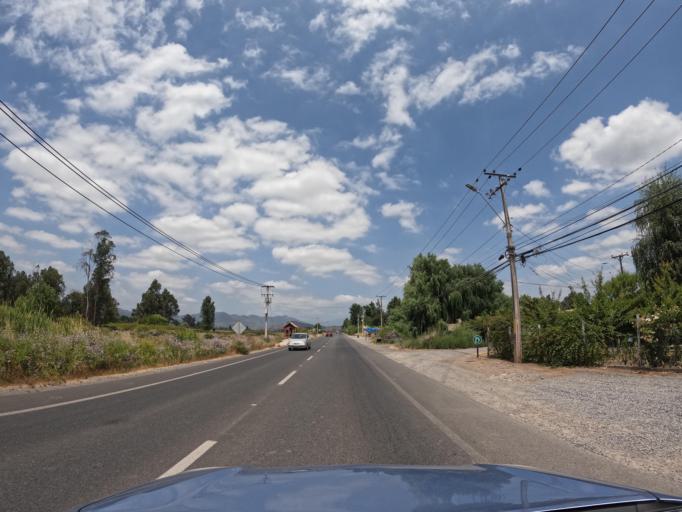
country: CL
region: Maule
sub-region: Provincia de Curico
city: Curico
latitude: -35.0163
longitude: -71.2141
